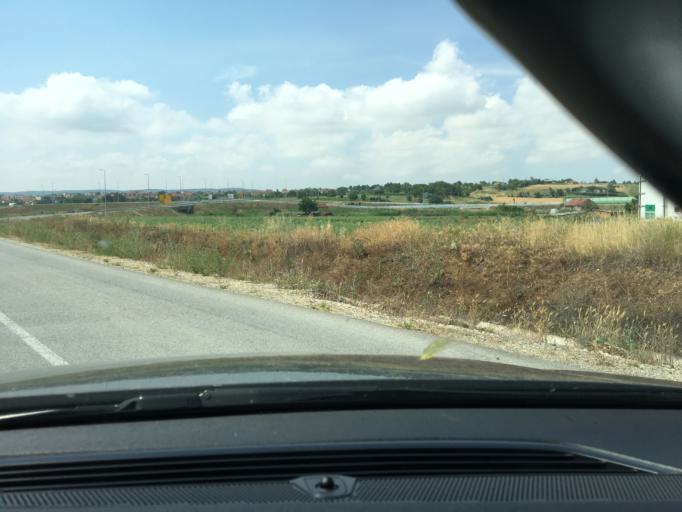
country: MK
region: Sveti Nikole
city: Sveti Nikole
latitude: 41.8807
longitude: 21.9395
